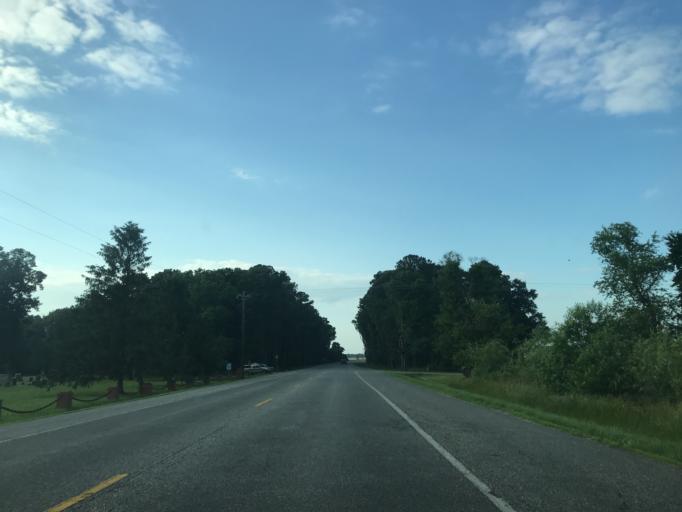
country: US
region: Maryland
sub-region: Caroline County
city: Denton
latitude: 38.8007
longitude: -75.7868
